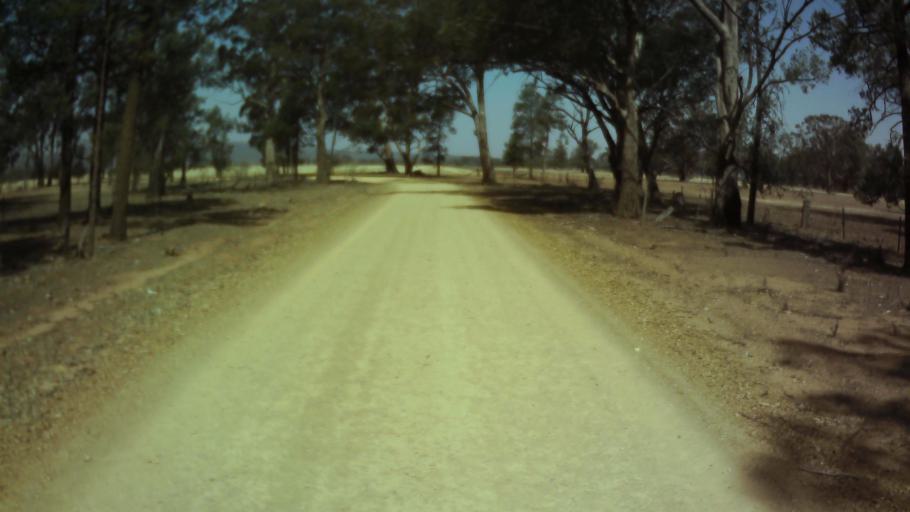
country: AU
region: New South Wales
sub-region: Weddin
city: Grenfell
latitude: -33.9962
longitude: 147.9242
